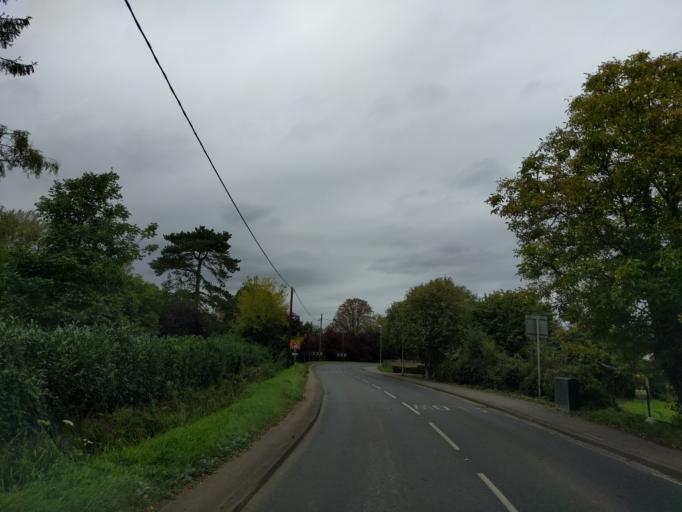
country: GB
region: England
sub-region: Cambridgeshire
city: Earith
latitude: 52.3048
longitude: 0.0527
